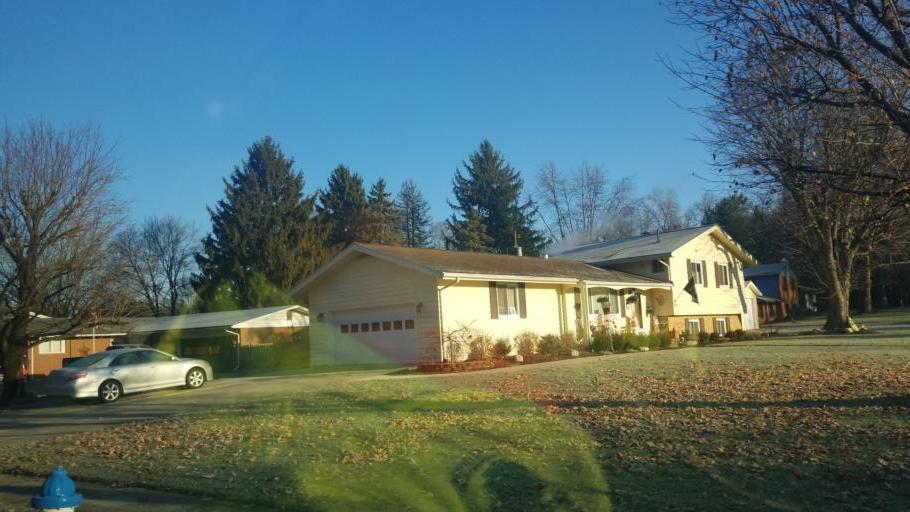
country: US
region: Ohio
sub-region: Marion County
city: Marion
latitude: 40.5772
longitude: -83.1011
